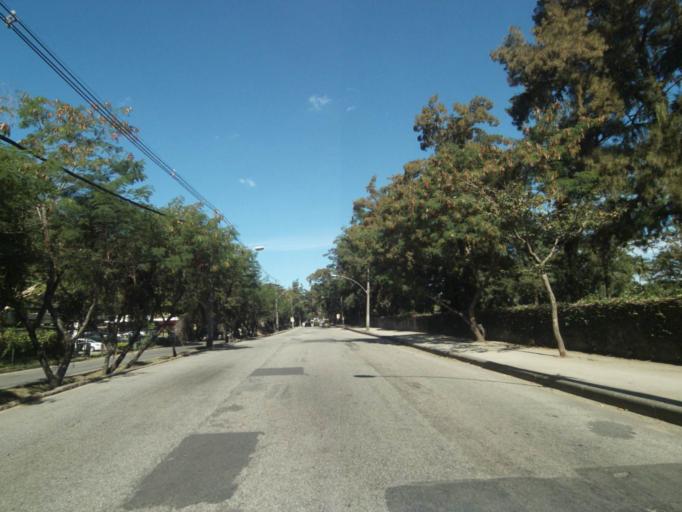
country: BR
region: Rio de Janeiro
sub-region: Rio De Janeiro
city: Rio de Janeiro
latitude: -22.9985
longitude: -43.3049
